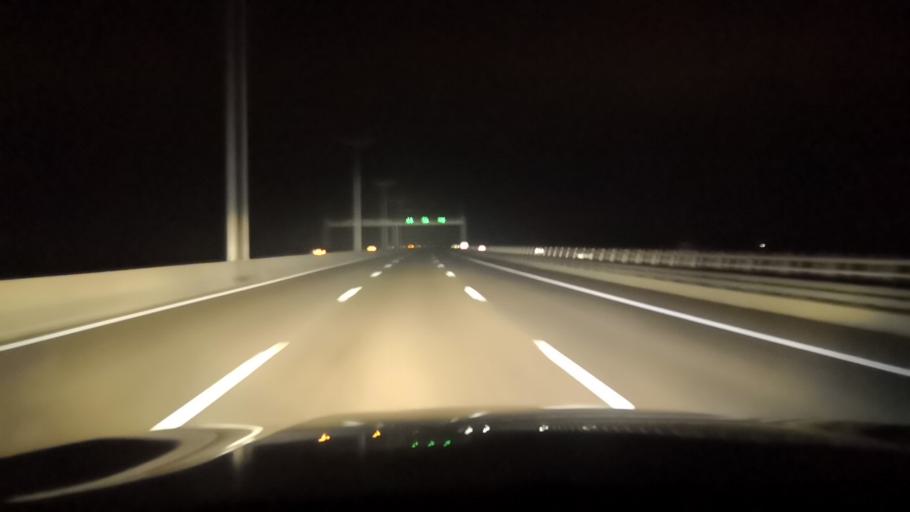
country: PT
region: Santarem
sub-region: Benavente
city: Samora Correia
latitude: 38.9975
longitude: -8.9014
